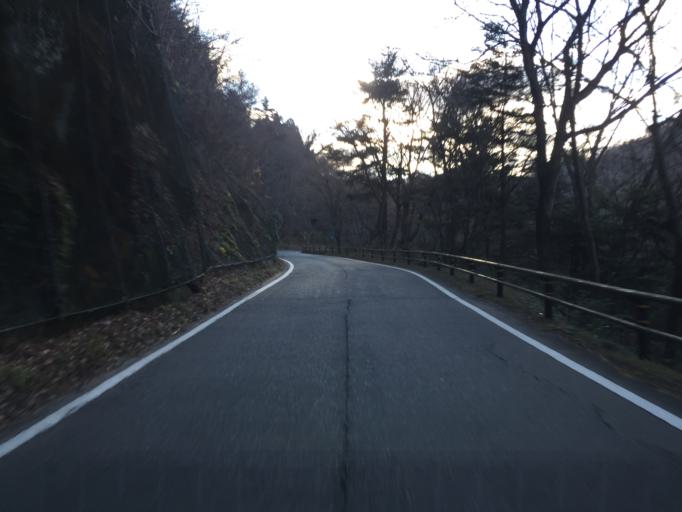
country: JP
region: Fukushima
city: Iwaki
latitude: 37.1628
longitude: 140.8274
